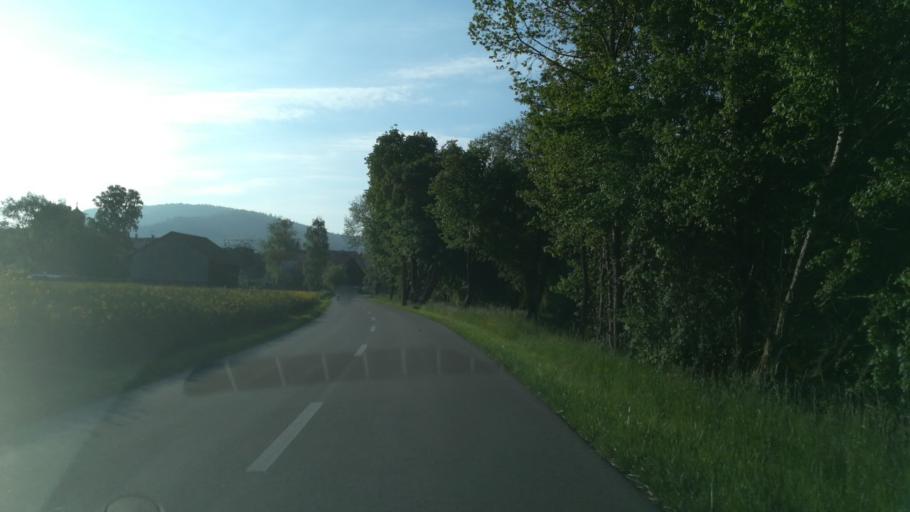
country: CH
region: Schaffhausen
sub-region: Bezirk Stein
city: Ramsen
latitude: 47.7084
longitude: 8.8057
